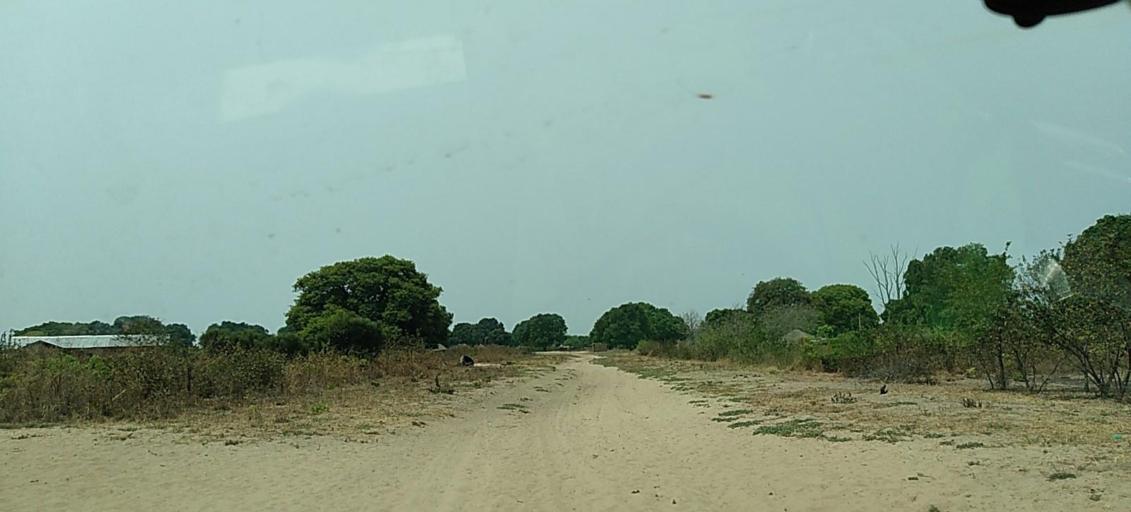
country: ZM
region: Western
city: Lukulu
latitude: -14.1575
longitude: 23.3084
